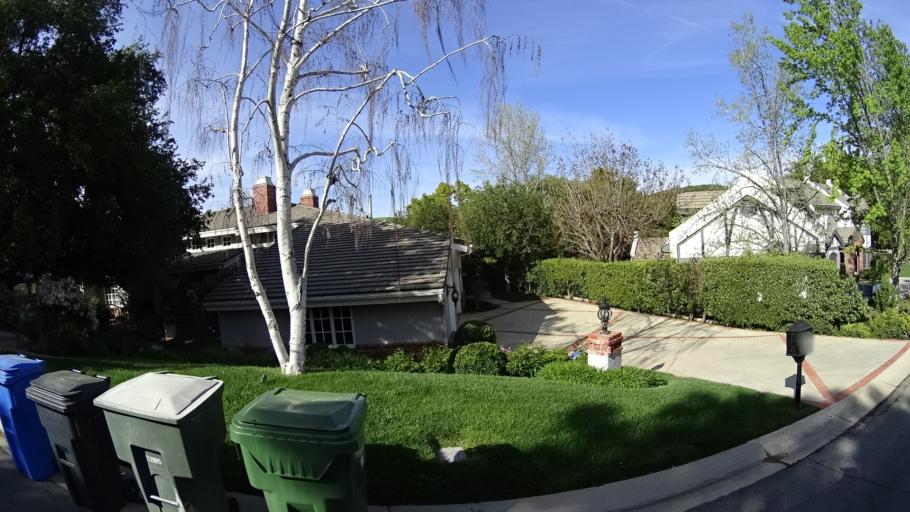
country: US
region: California
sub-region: Ventura County
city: Oak Park
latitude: 34.1929
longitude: -118.7912
